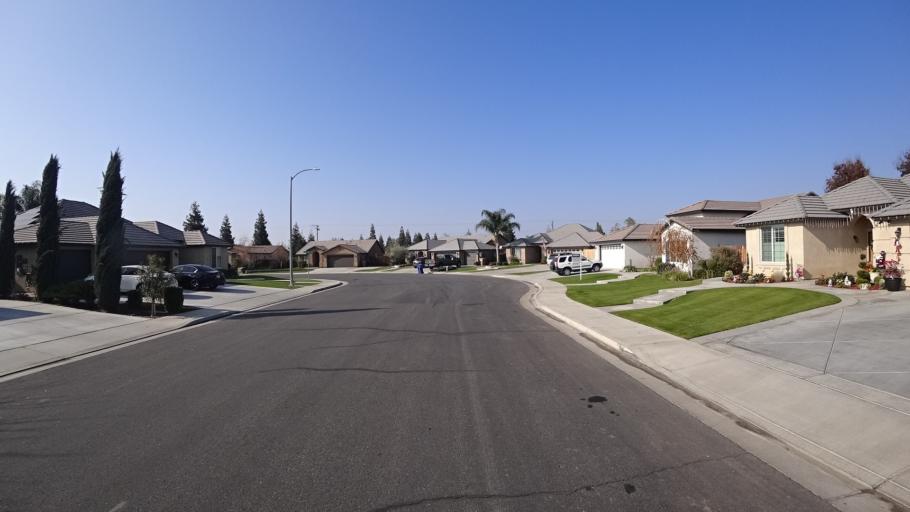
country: US
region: California
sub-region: Kern County
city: Greenacres
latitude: 35.4153
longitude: -119.1265
